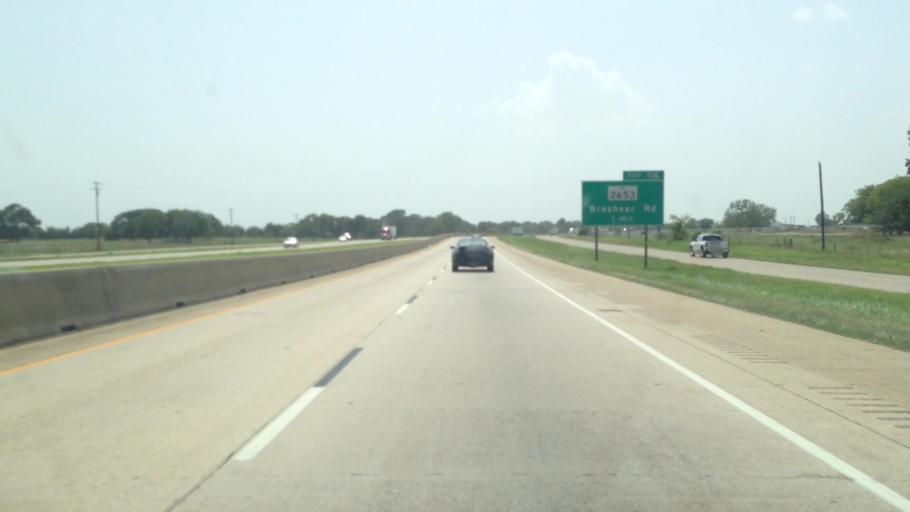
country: US
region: Texas
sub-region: Hopkins County
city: Sulphur Springs
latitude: 33.1201
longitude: -95.7143
